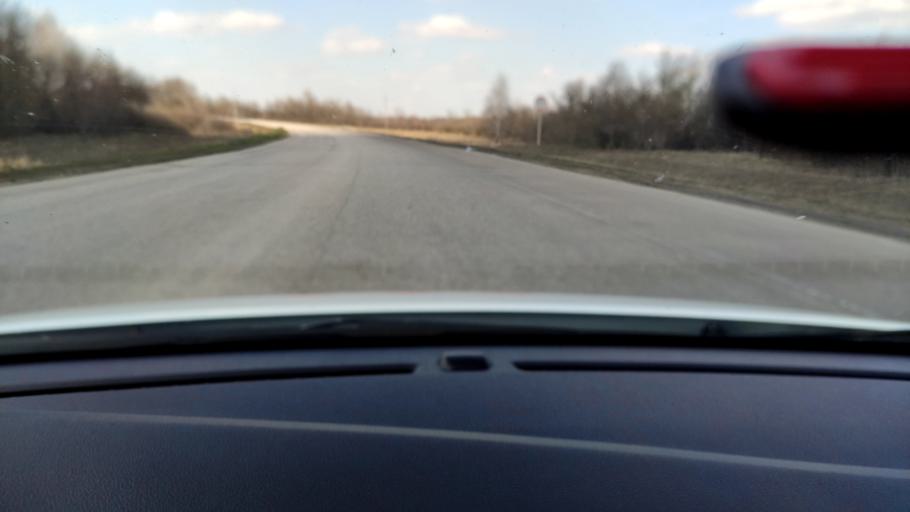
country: RU
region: Voronezj
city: Kolodeznyy
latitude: 51.3044
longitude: 39.0393
